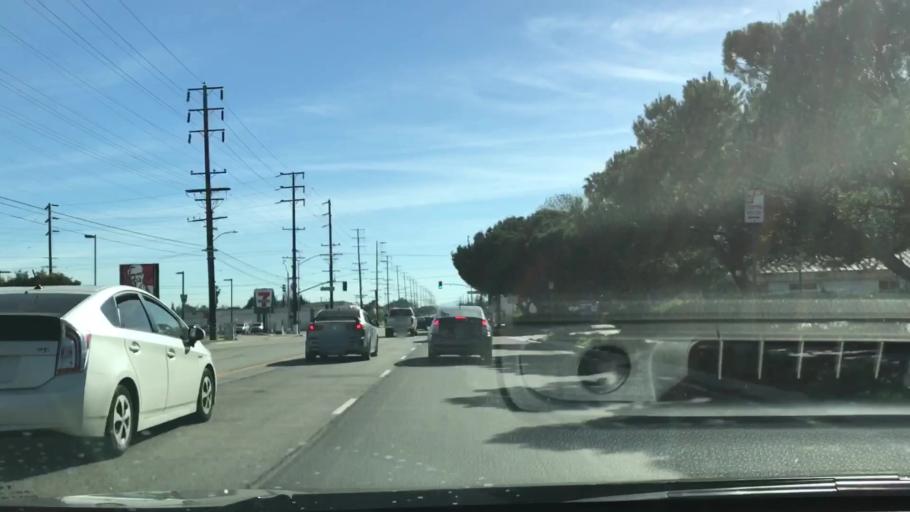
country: US
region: California
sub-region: Los Angeles County
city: Alondra Park
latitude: 33.8813
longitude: -118.3266
